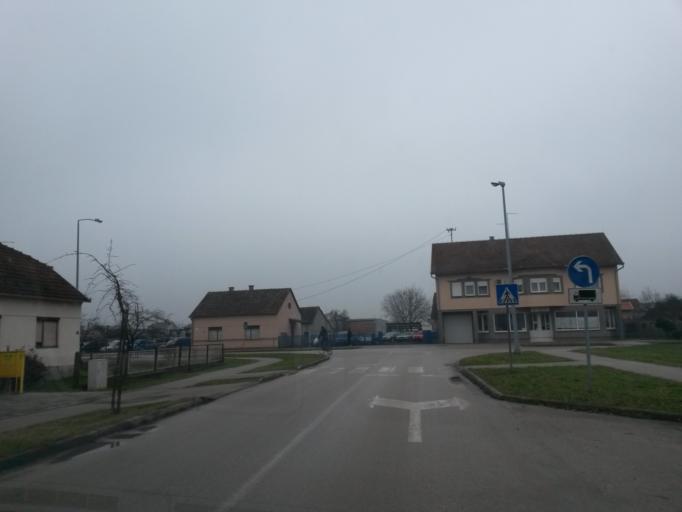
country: HR
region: Vukovarsko-Srijemska
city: Zupanja
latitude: 45.0777
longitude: 18.6960
